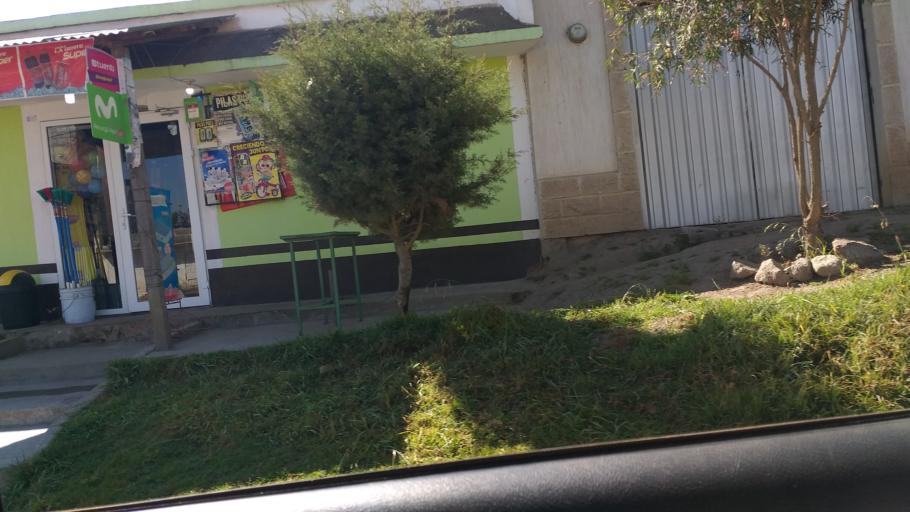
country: GT
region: Quetzaltenango
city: Quetzaltenango
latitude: 14.7992
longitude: -91.5474
